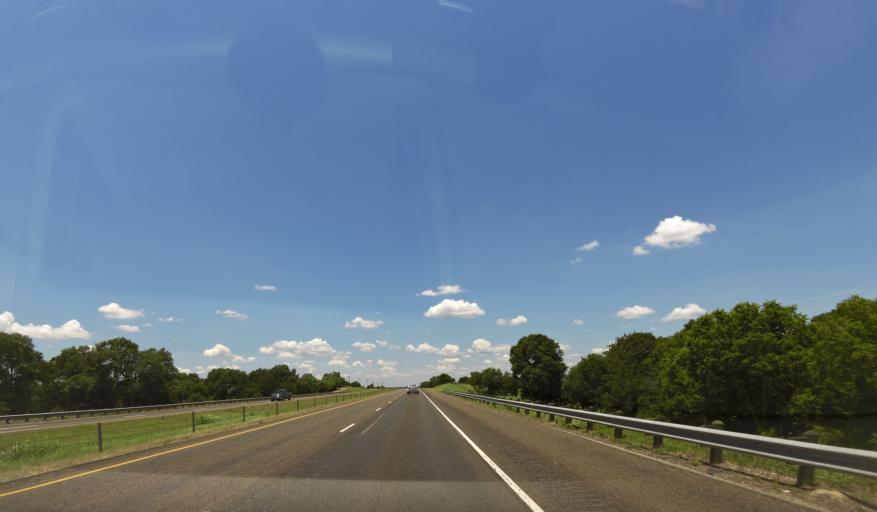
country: US
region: Texas
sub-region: Washington County
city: Brenham
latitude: 30.1851
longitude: -96.4904
